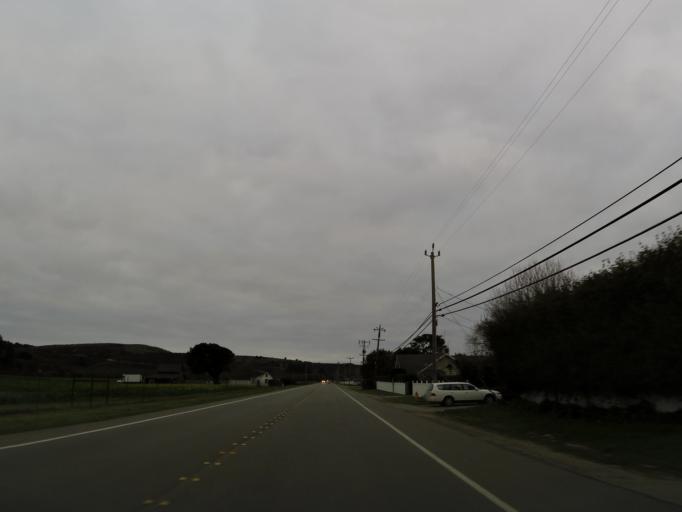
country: US
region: California
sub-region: San Mateo County
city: Portola Valley
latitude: 37.2513
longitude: -122.3857
